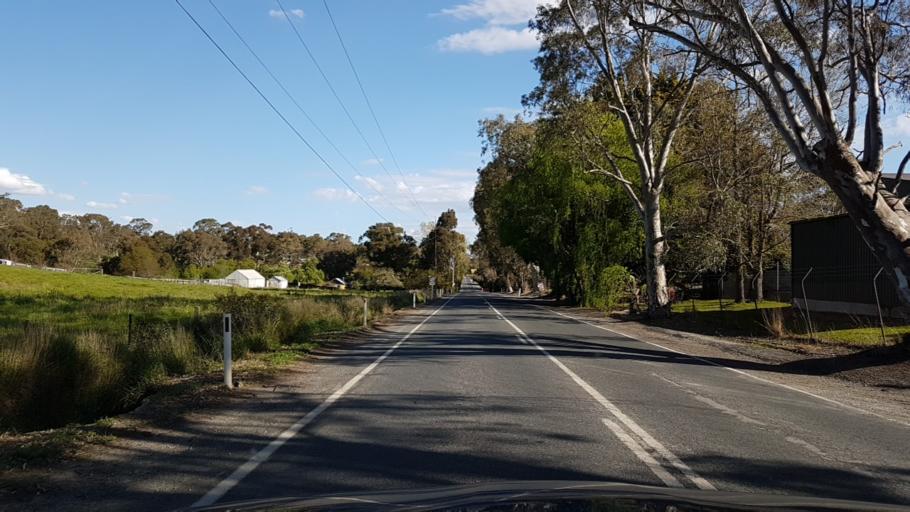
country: AU
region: South Australia
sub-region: Adelaide Hills
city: Lobethal
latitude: -34.8916
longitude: 138.8793
